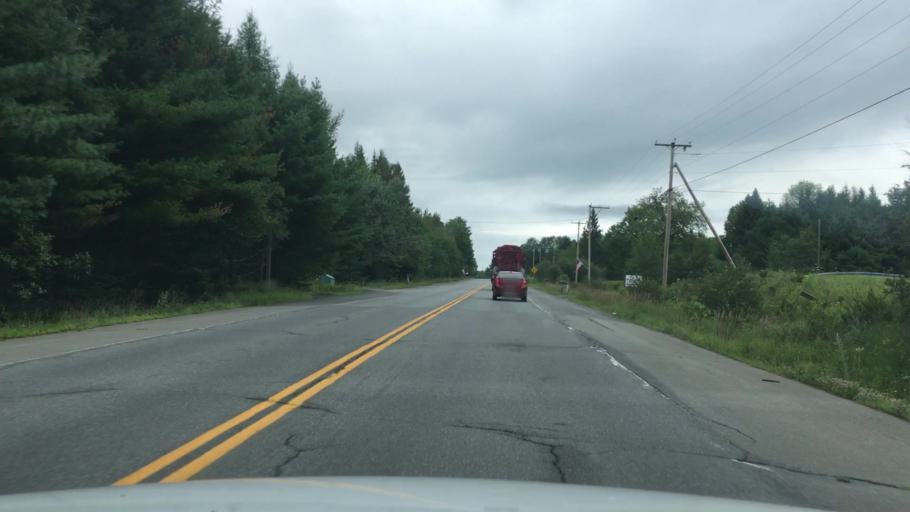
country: US
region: Maine
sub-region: Hancock County
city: Franklin
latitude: 44.8370
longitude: -68.3518
